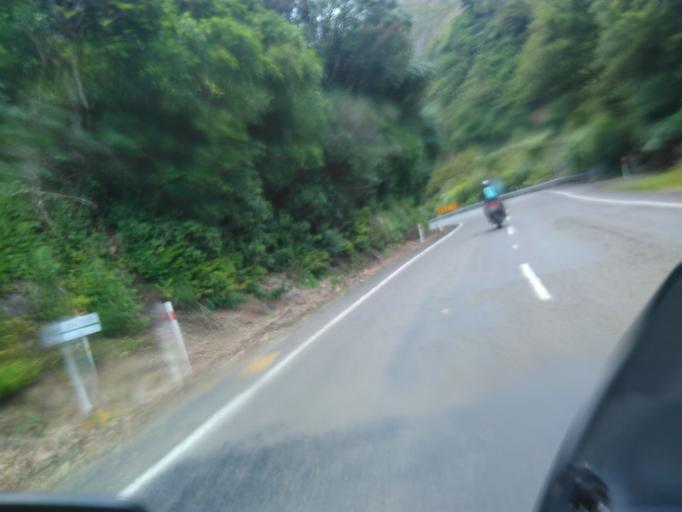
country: NZ
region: Bay of Plenty
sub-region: Opotiki District
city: Opotiki
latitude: -38.2682
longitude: 177.3063
